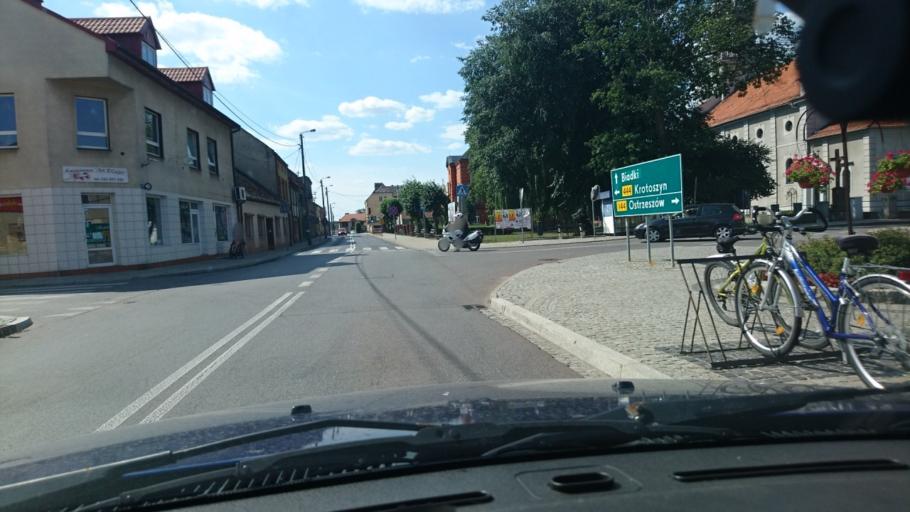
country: PL
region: Greater Poland Voivodeship
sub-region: Powiat krotoszynski
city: Sulmierzyce
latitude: 51.6059
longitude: 17.5312
